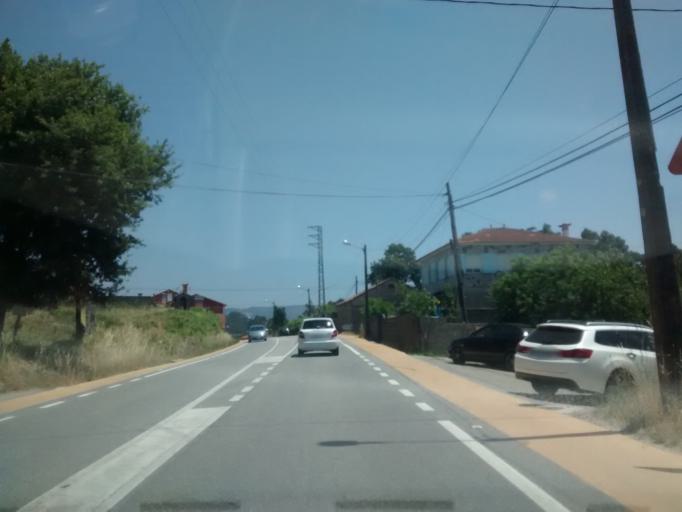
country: ES
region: Galicia
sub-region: Provincia de Pontevedra
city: Nigran
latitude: 42.1139
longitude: -8.7942
